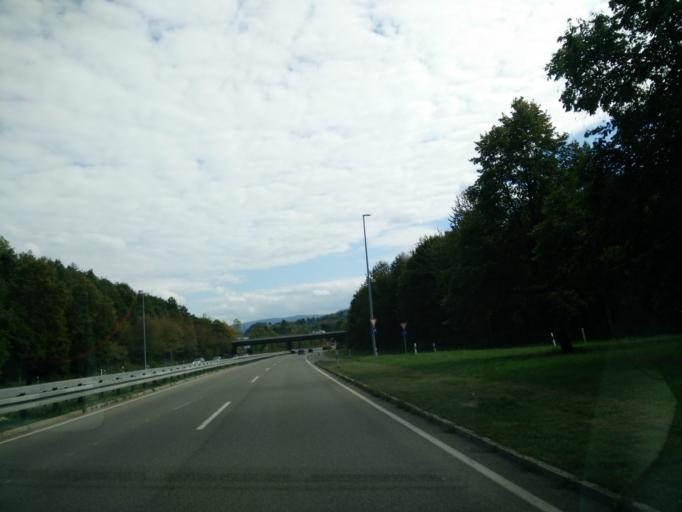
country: DE
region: Baden-Wuerttemberg
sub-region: Tuebingen Region
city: Wannweil
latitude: 48.4975
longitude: 9.1624
